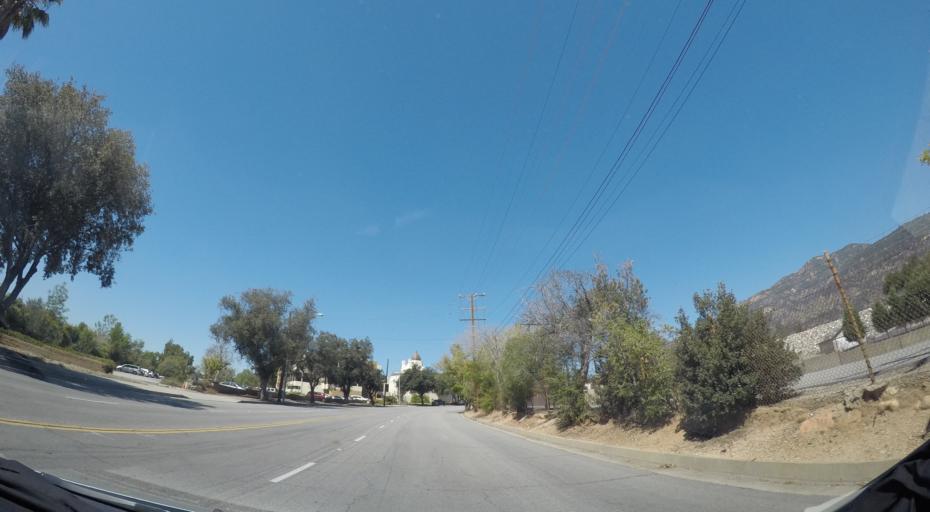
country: US
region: California
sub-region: Los Angeles County
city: East Pasadena
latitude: 34.1674
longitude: -118.0933
